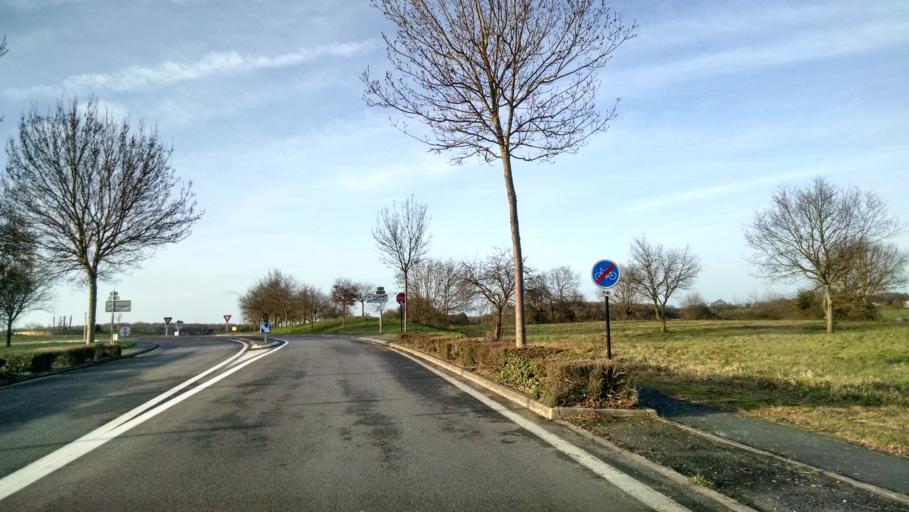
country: FR
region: Pays de la Loire
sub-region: Departement de la Vendee
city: Saint-Hilaire-de-Loulay
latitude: 47.0085
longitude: -1.3367
